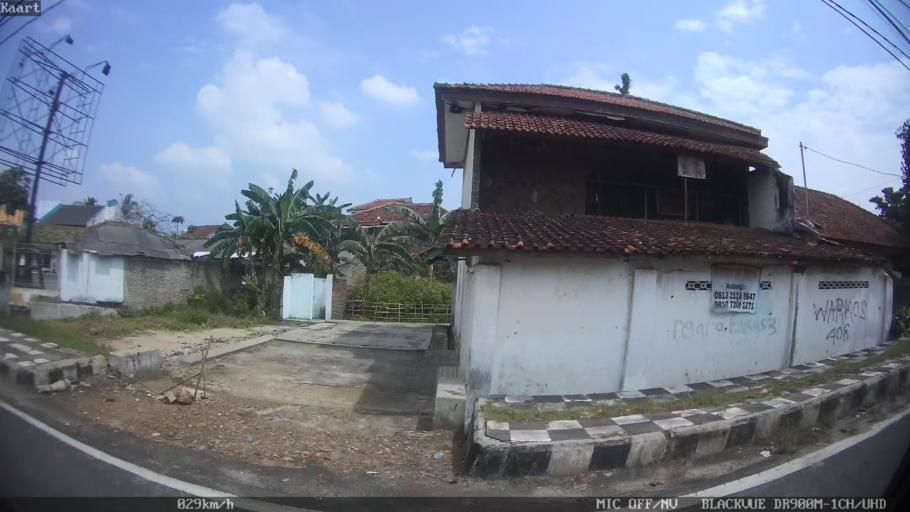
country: ID
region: Lampung
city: Bandarlampung
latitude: -5.4338
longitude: 105.2561
